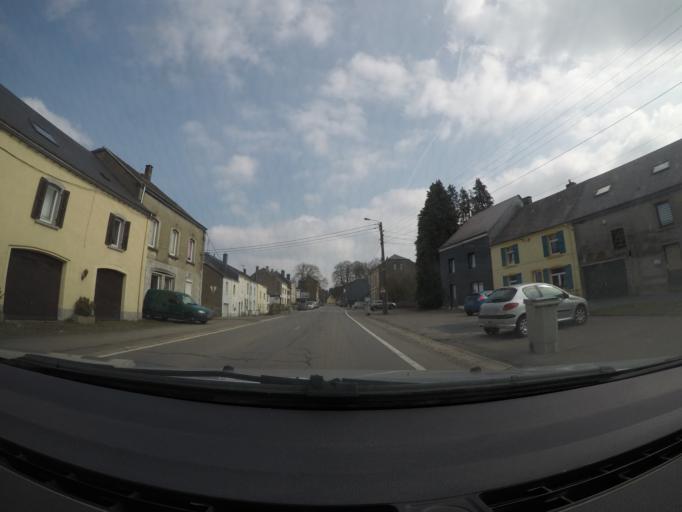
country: BE
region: Wallonia
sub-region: Province du Luxembourg
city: Tintigny
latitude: 49.7250
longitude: 5.5369
